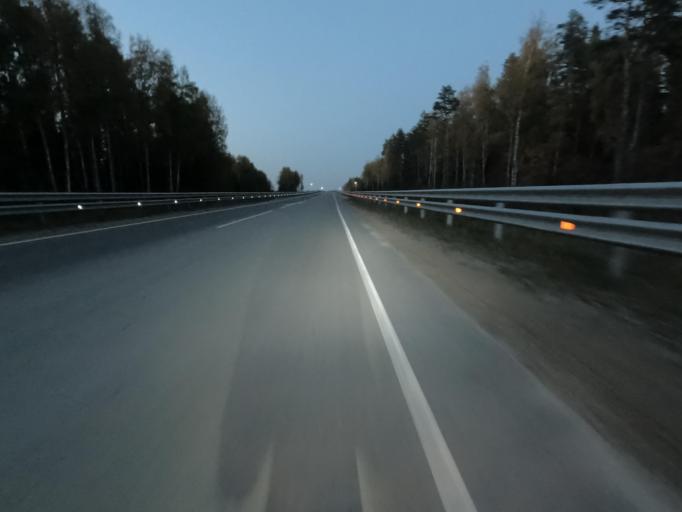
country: RU
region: Leningrad
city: Lyuban'
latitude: 59.1944
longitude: 31.2538
